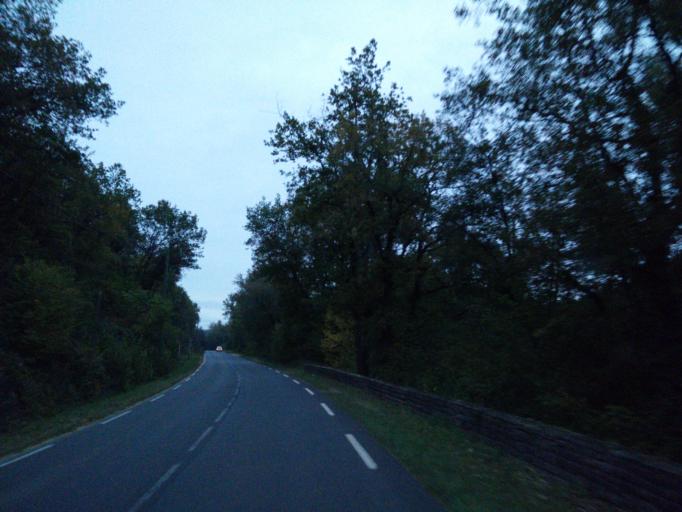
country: FR
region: Aquitaine
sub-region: Departement de la Dordogne
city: Saint-Cyprien
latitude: 44.9361
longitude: 1.0663
